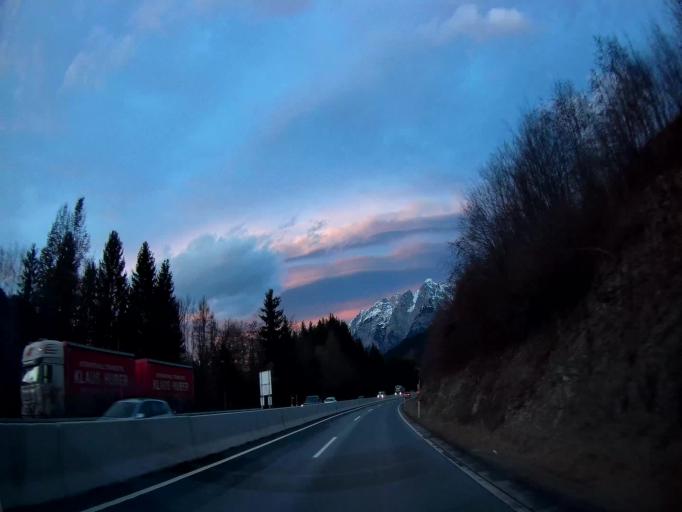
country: AT
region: Salzburg
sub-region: Politischer Bezirk Sankt Johann im Pongau
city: Bischofshofen
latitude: 47.4282
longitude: 13.2242
